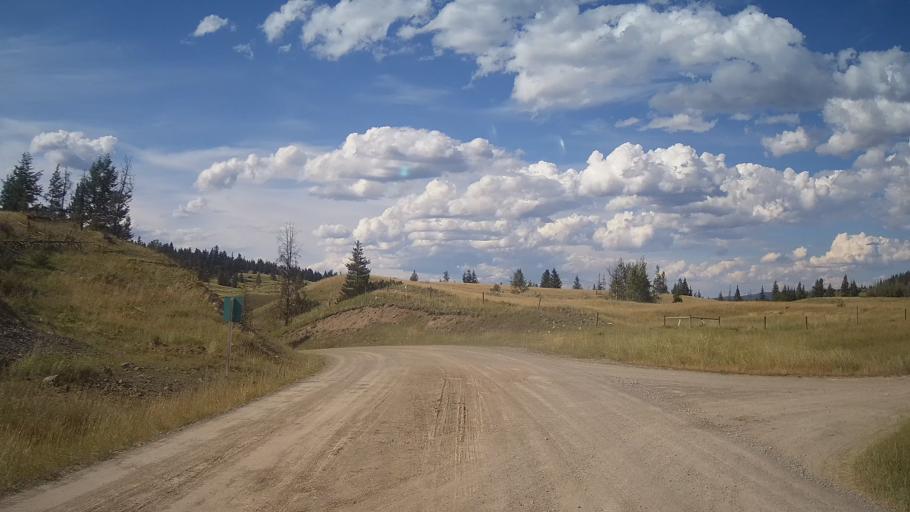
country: CA
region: British Columbia
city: Lillooet
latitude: 51.3017
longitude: -121.9842
